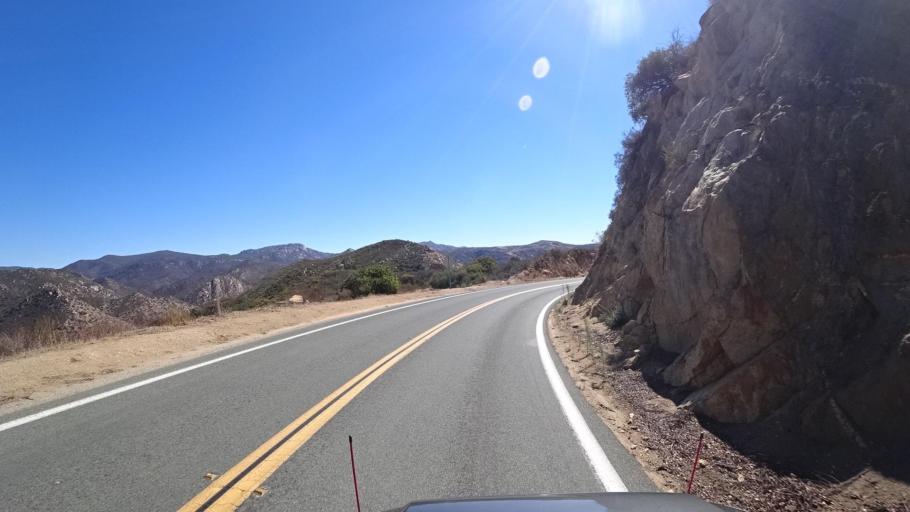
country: US
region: California
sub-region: San Diego County
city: Descanso
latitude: 32.7496
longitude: -116.6667
